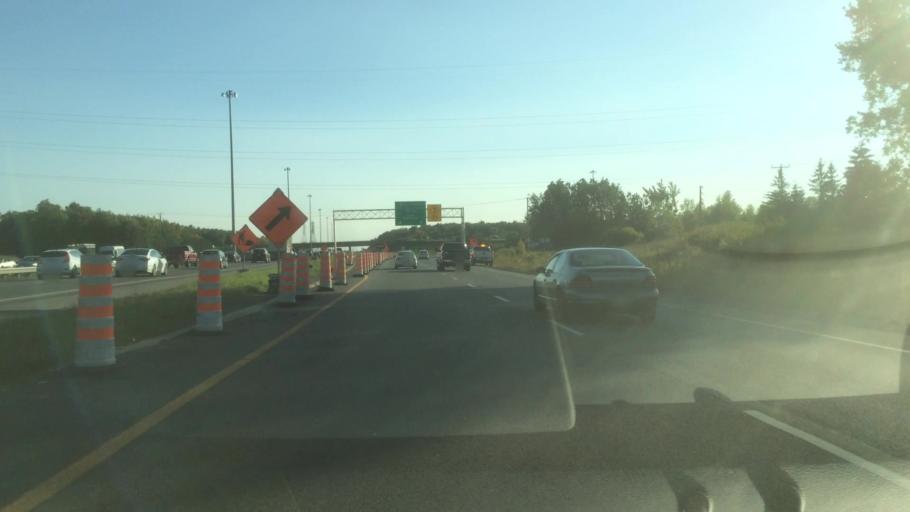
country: CA
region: Quebec
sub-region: Laurentides
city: Boisbriand
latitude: 45.6038
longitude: -73.8595
